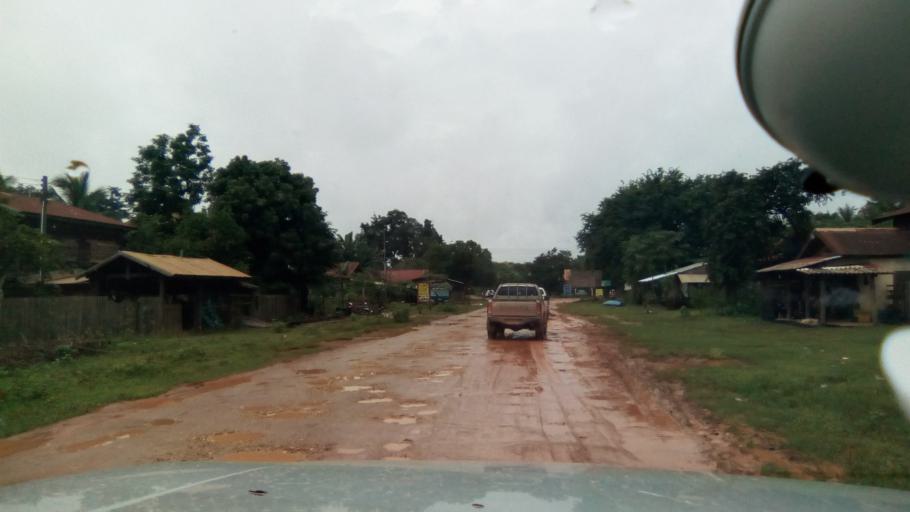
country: LA
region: Attapu
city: Attapu
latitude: 14.6757
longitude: 106.5781
